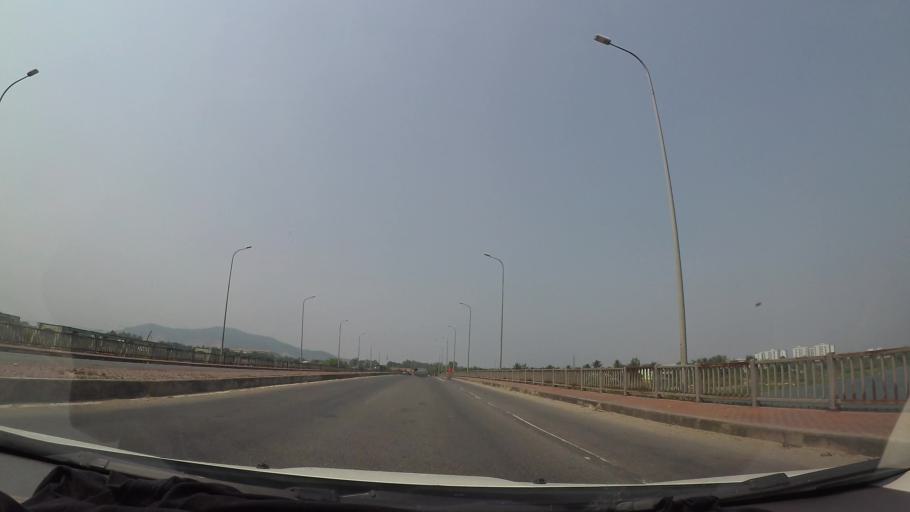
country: VN
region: Da Nang
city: Cam Le
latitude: 15.9987
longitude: 108.1912
